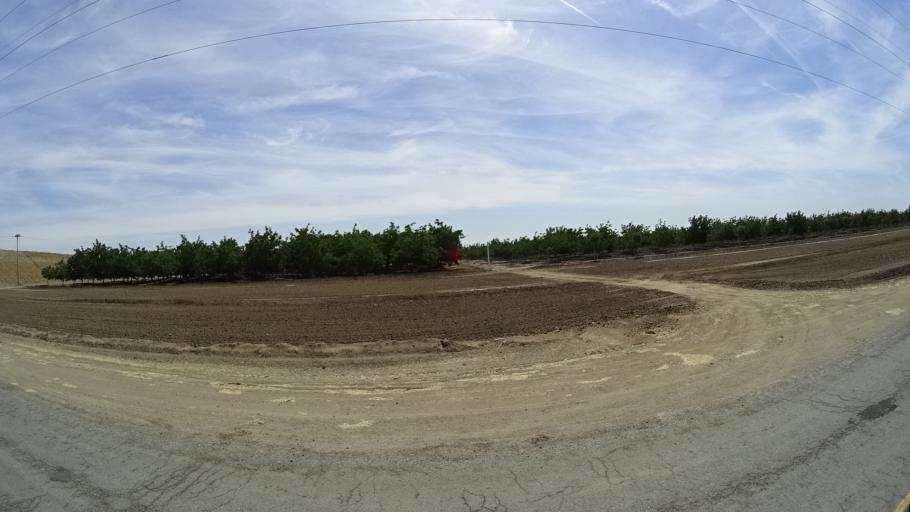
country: US
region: California
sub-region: Kings County
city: Hanford
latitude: 36.3563
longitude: -119.5920
